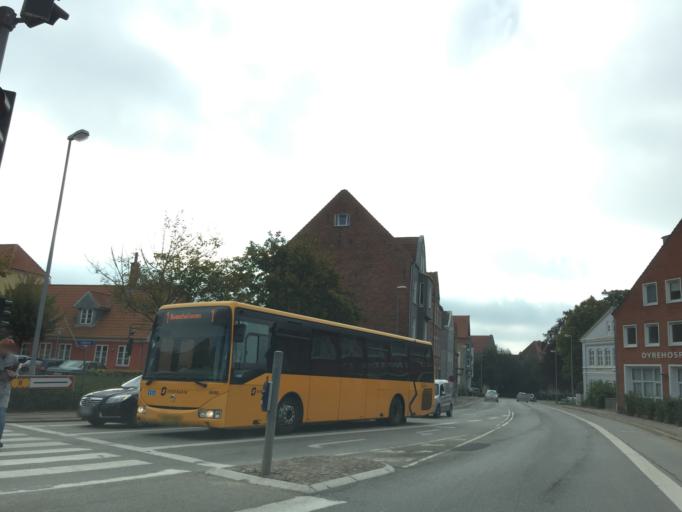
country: DK
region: South Denmark
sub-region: Sonderborg Kommune
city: Sonderborg
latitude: 54.9132
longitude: 9.7911
